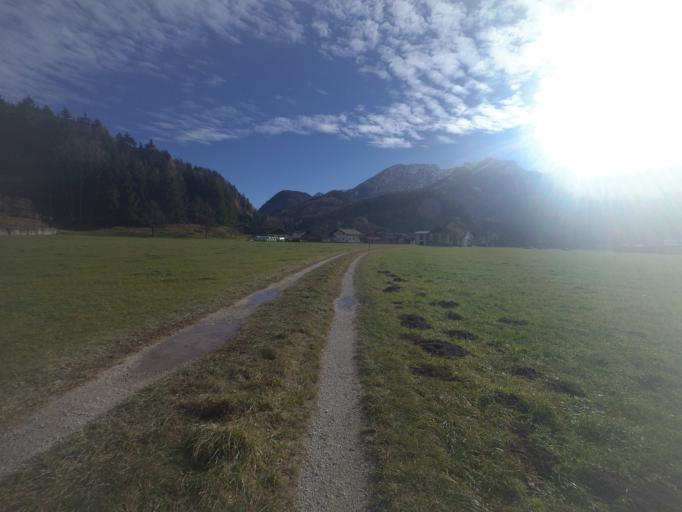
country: AT
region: Salzburg
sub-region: Politischer Bezirk Hallein
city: Golling an der Salzach
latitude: 47.5931
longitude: 13.1816
